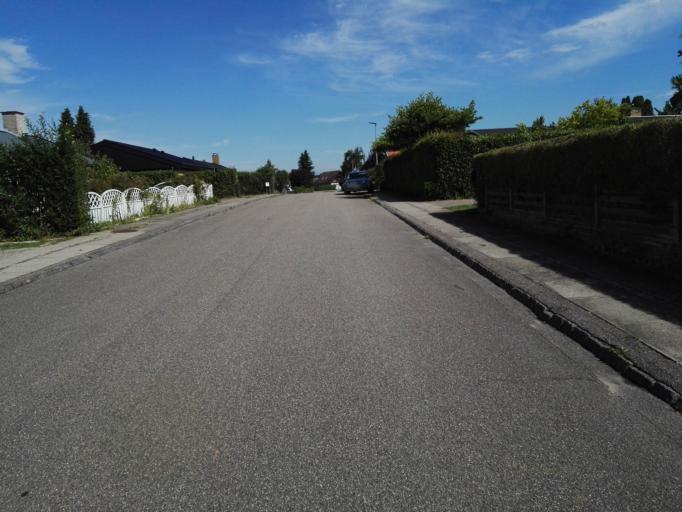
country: DK
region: Capital Region
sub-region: Egedal Kommune
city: Olstykke
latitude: 55.7951
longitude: 12.1432
